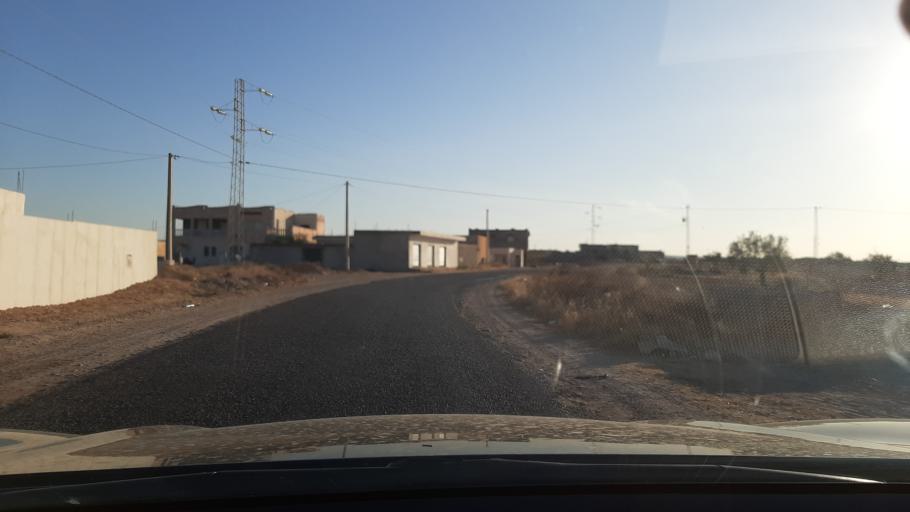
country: TN
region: Qabis
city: Matmata
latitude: 33.6164
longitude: 10.2485
